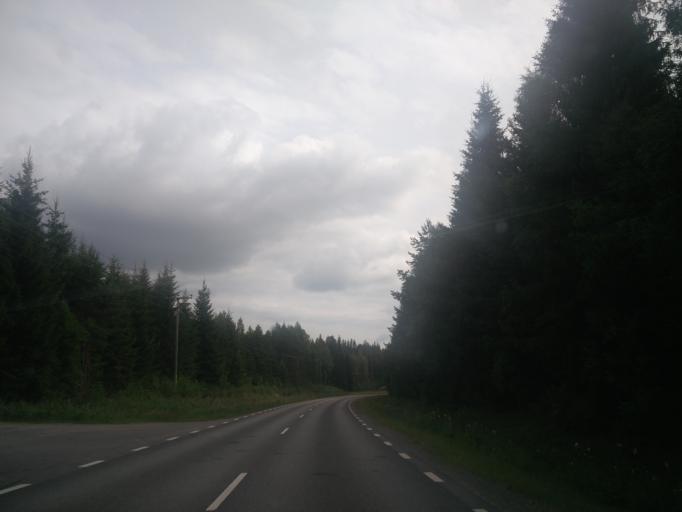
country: SE
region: Vaermland
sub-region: Arvika Kommun
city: Arvika
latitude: 59.7236
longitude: 12.5676
